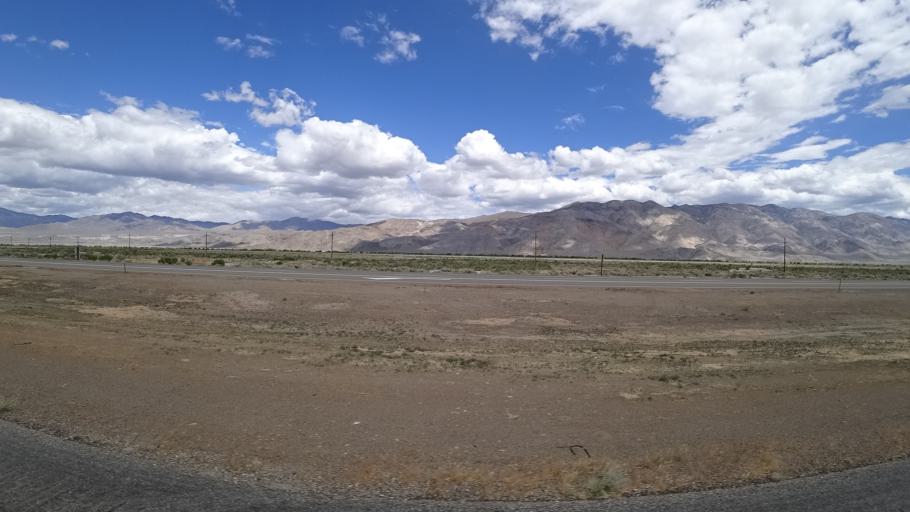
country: US
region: California
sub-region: Inyo County
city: Big Pine
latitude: 37.1050
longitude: -118.2529
